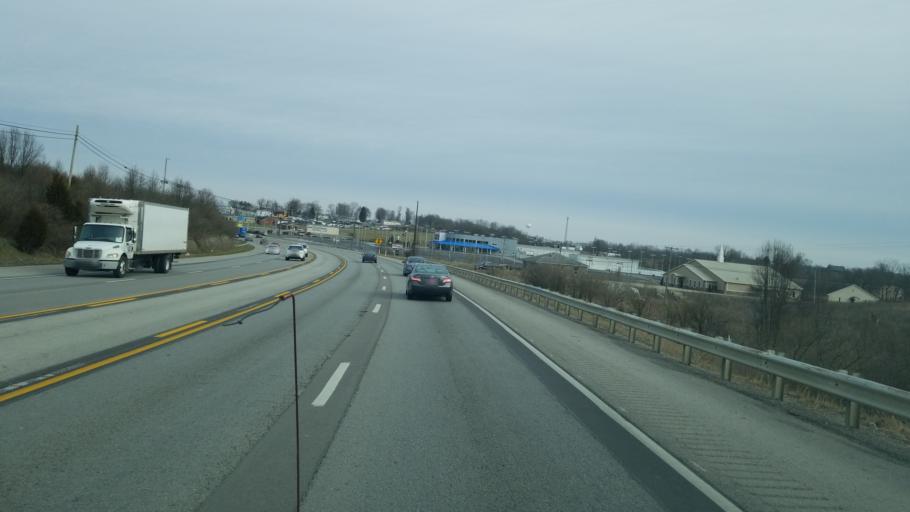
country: US
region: Kentucky
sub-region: Jessamine County
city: Nicholasville
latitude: 37.9259
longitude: -84.5510
